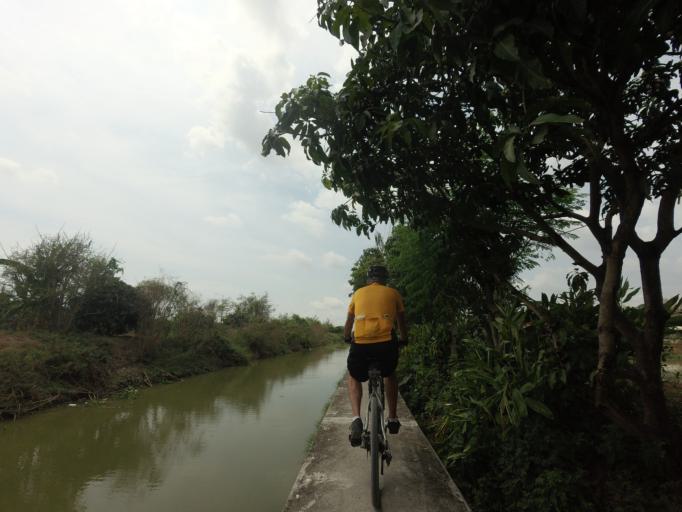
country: TH
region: Bangkok
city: Lat Krabang
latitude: 13.6817
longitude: 100.7691
